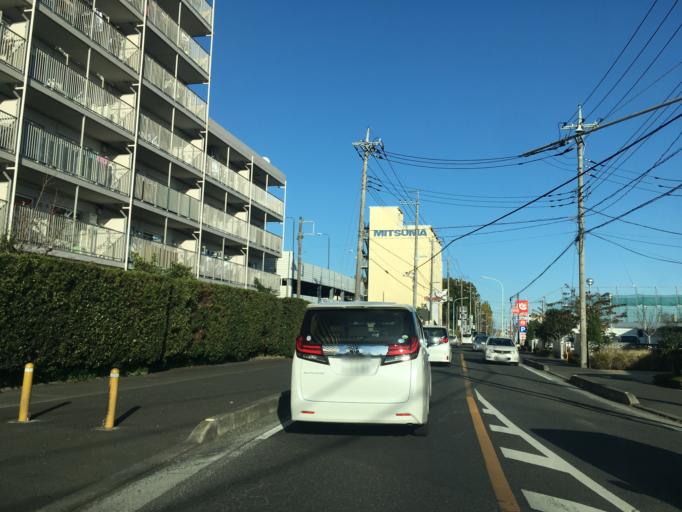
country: JP
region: Saitama
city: Tokorozawa
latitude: 35.8028
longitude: 139.4808
